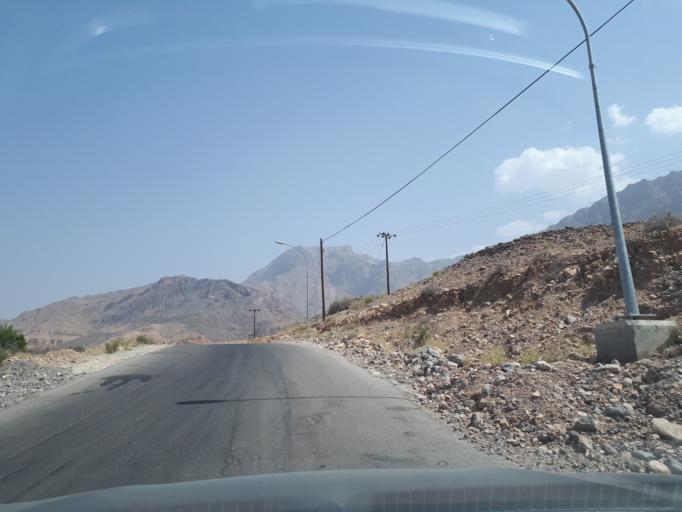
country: OM
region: Ash Sharqiyah
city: Ibra'
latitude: 23.0849
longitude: 58.8646
